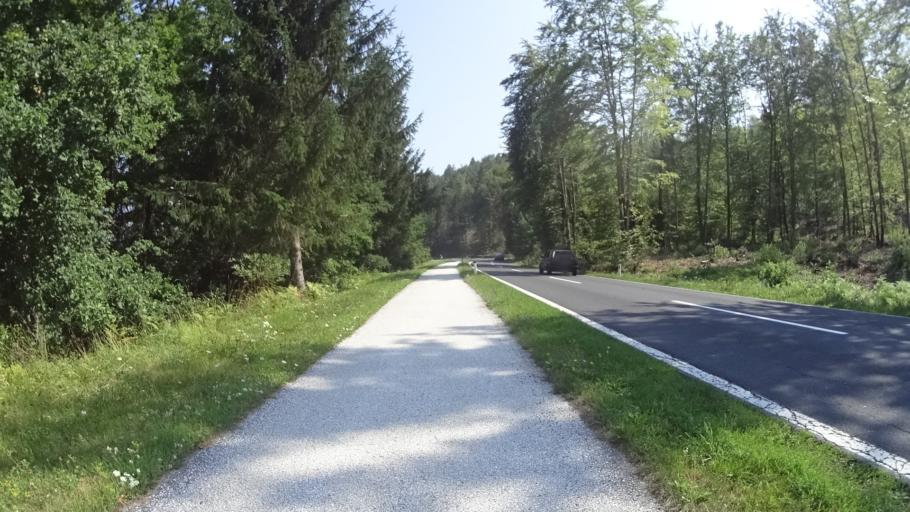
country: AT
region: Carinthia
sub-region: Politischer Bezirk Volkermarkt
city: Sittersdorf
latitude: 46.5582
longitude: 14.6213
